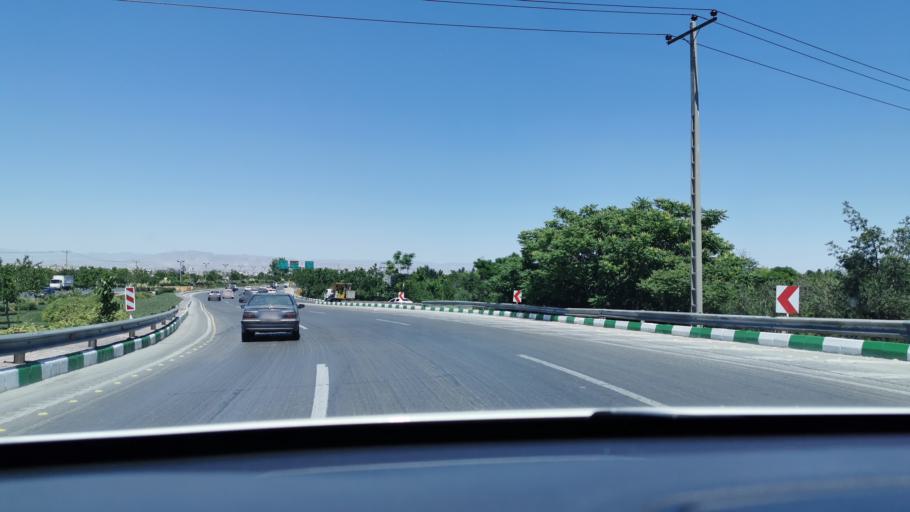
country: IR
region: Razavi Khorasan
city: Mashhad
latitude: 36.2498
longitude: 59.6110
